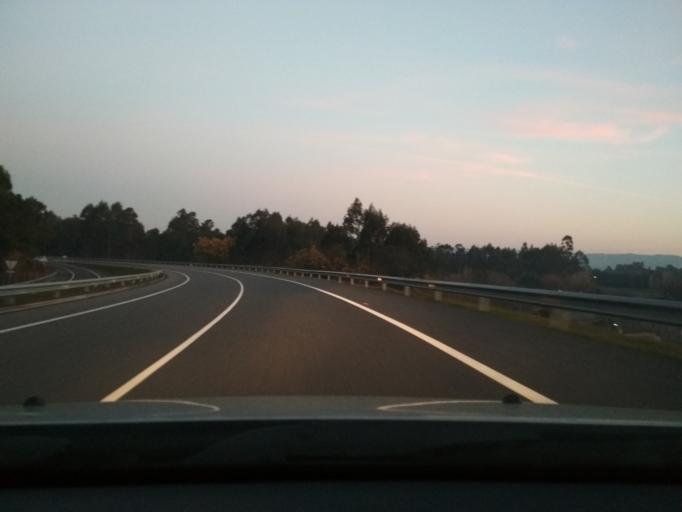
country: ES
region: Galicia
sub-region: Provincia da Coruna
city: Santiago de Compostela
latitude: 42.8467
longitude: -8.5939
